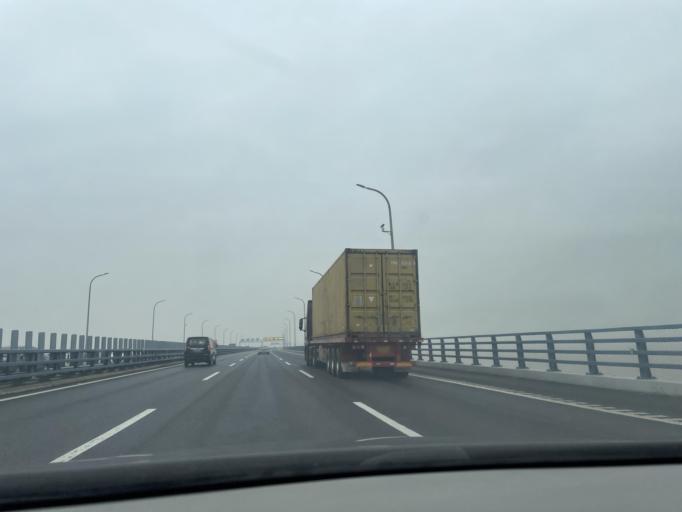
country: CN
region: Zhejiang Sheng
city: Zhapu
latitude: 30.4940
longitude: 121.0920
